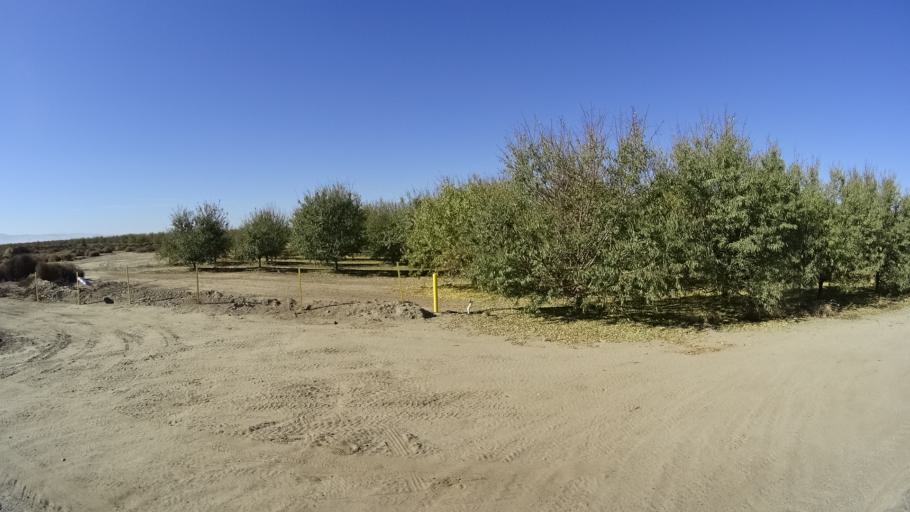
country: US
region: California
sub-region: Kern County
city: Greenfield
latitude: 35.2558
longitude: -119.0567
